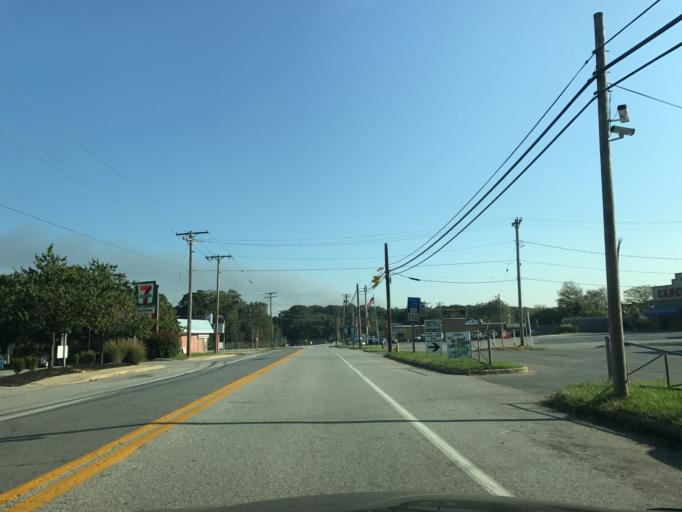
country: US
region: Maryland
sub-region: Anne Arundel County
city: Severn
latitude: 39.1590
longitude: -76.6839
